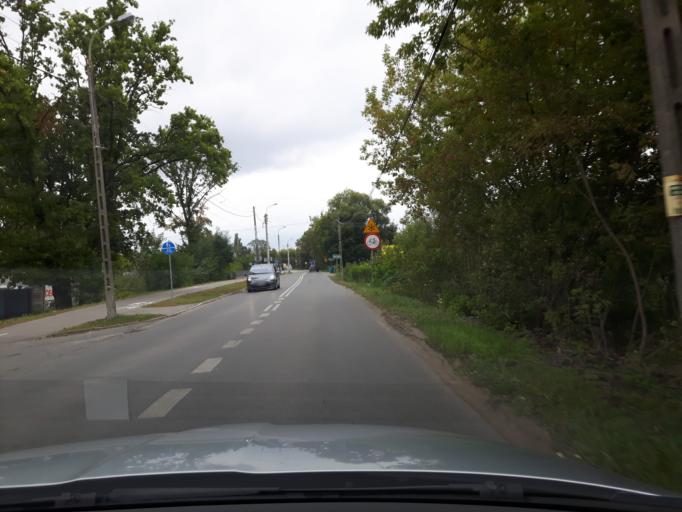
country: PL
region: Masovian Voivodeship
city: Zielonka
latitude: 52.3135
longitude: 21.1853
